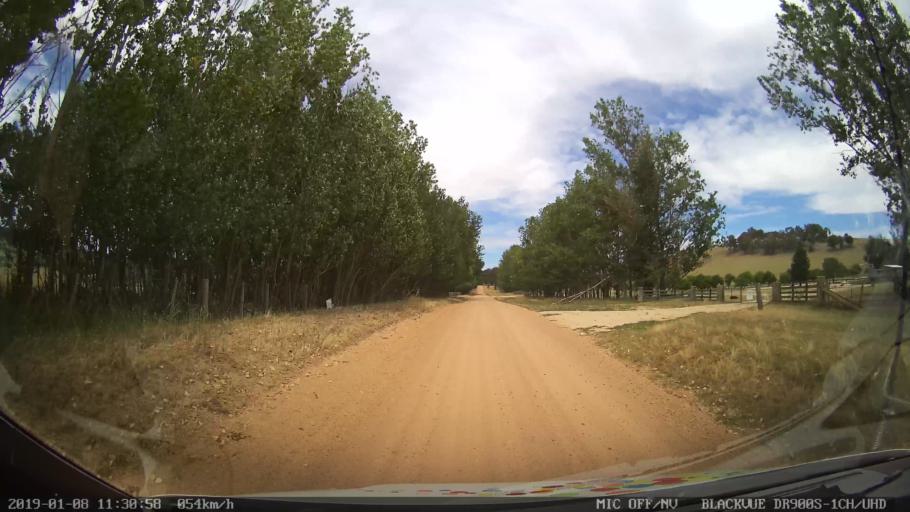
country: AU
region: New South Wales
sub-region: Guyra
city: Guyra
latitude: -30.3103
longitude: 151.5412
